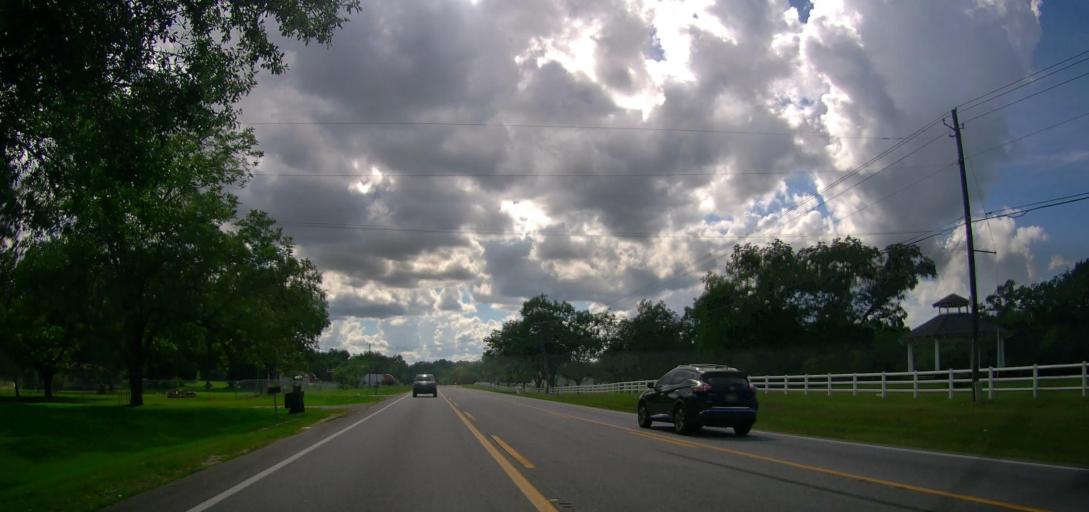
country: US
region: Alabama
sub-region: Russell County
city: Ladonia
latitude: 32.4566
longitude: -85.1907
